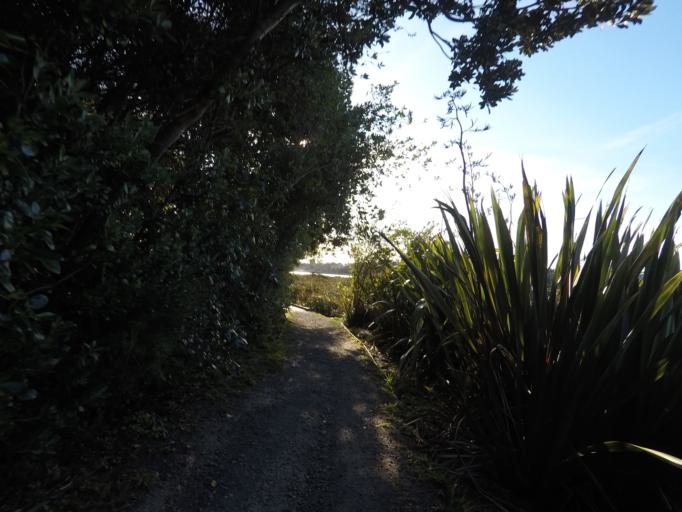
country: NZ
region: Auckland
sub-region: Auckland
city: Rosebank
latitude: -36.8243
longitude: 174.6486
